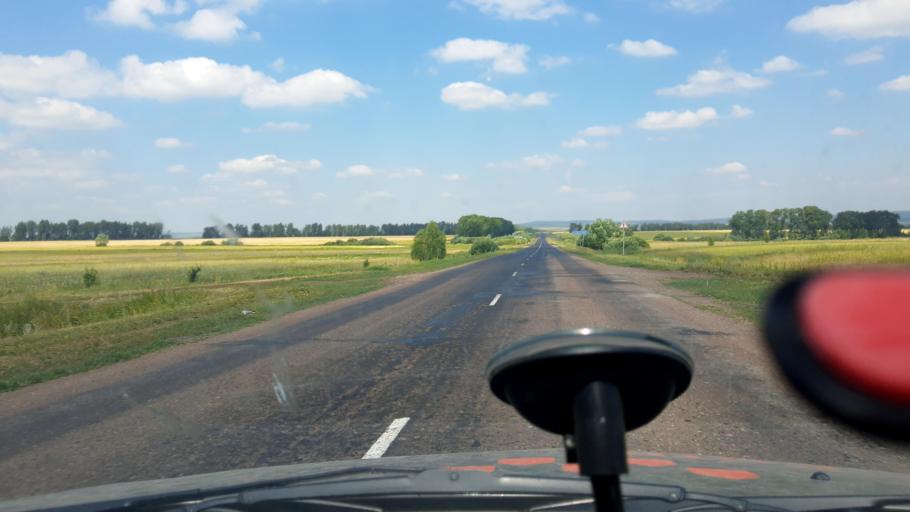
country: RU
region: Bashkortostan
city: Chekmagush
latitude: 54.8643
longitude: 54.5695
